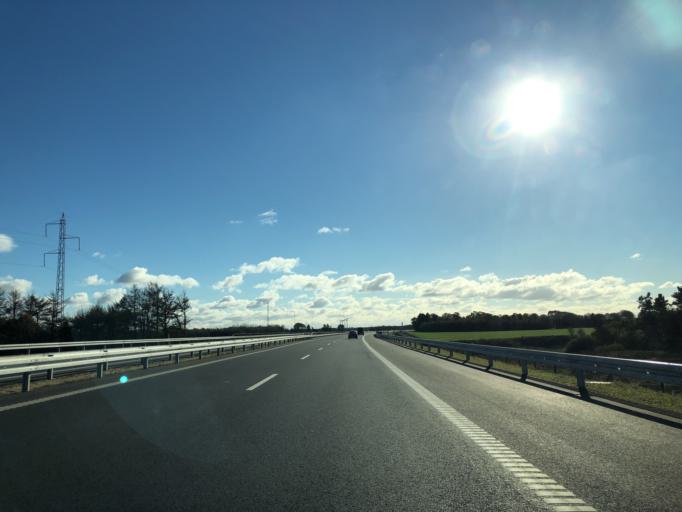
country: DK
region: Central Jutland
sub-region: Herning Kommune
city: Avlum
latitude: 56.3600
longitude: 8.7311
